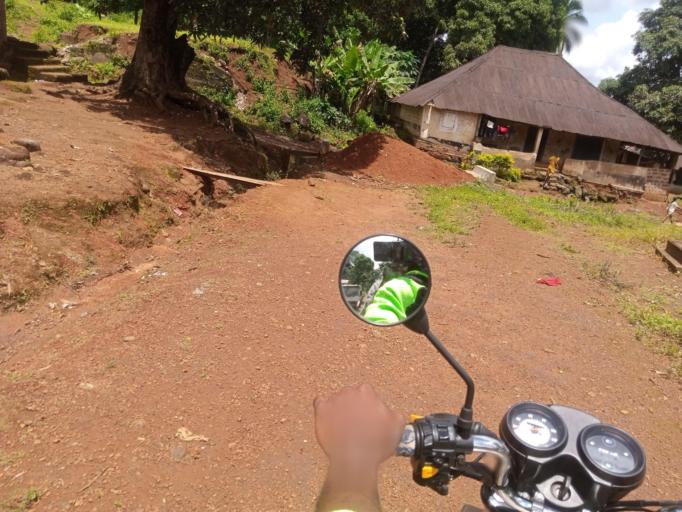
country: SL
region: Northern Province
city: Port Loko
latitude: 8.7614
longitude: -12.7895
